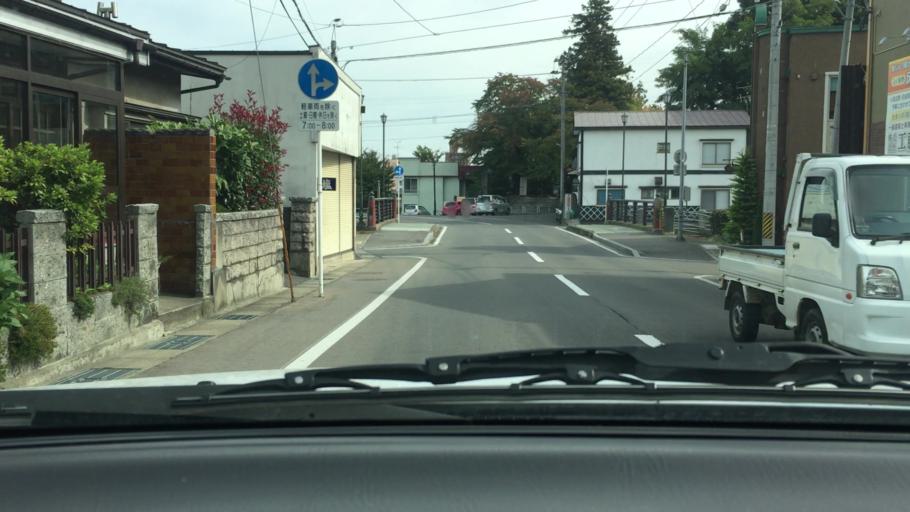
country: JP
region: Aomori
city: Hirosaki
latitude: 40.5971
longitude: 140.4672
